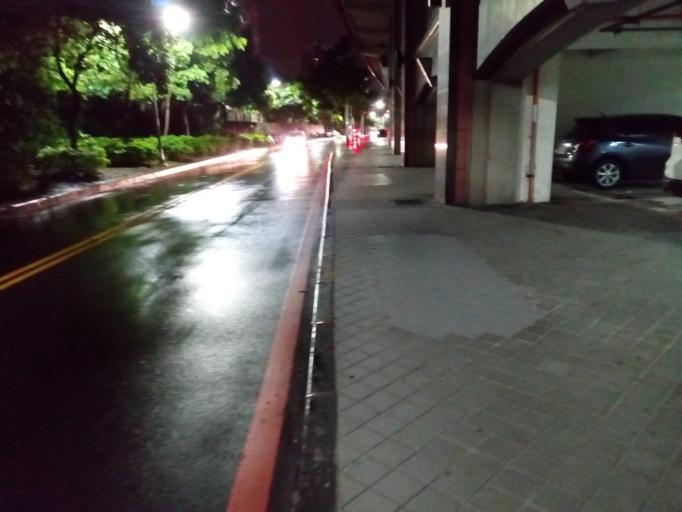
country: TW
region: Taiwan
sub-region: Keelung
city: Keelung
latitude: 25.0669
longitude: 121.6603
